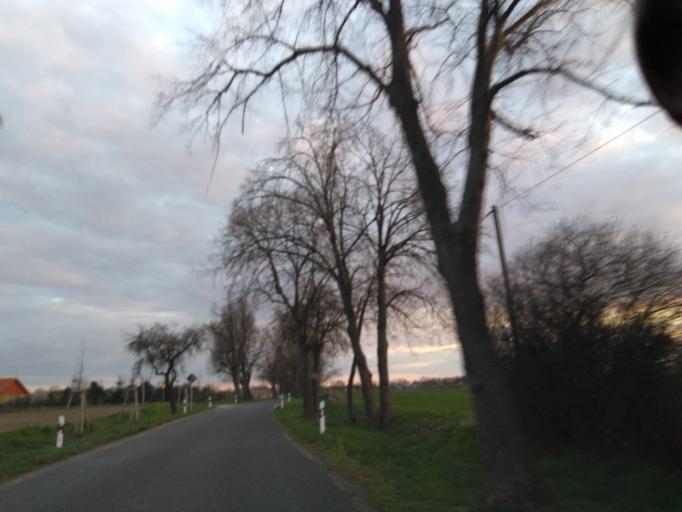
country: DE
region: Brandenburg
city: Protzel
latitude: 52.6581
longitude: 14.0698
